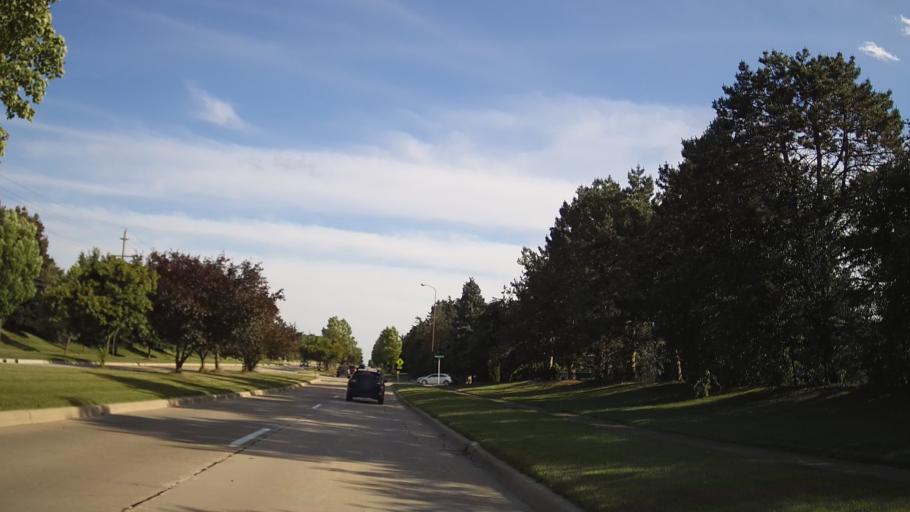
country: US
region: Michigan
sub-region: Oakland County
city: Troy
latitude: 42.5852
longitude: -83.1882
